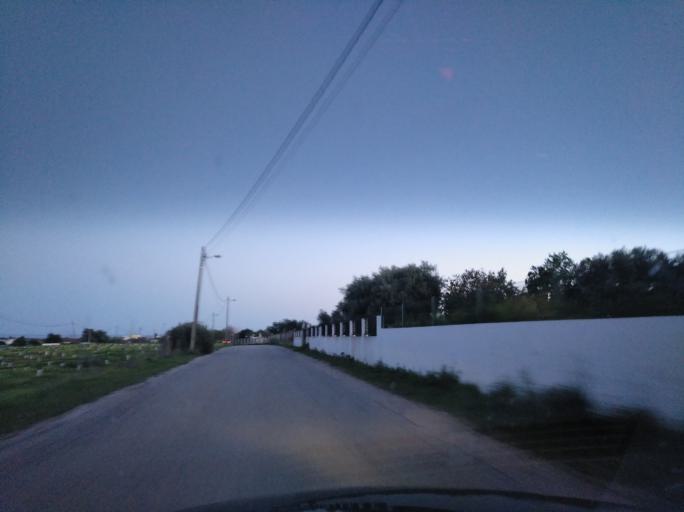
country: PT
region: Faro
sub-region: Vila Real de Santo Antonio
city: Monte Gordo
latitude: 37.1869
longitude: -7.5092
